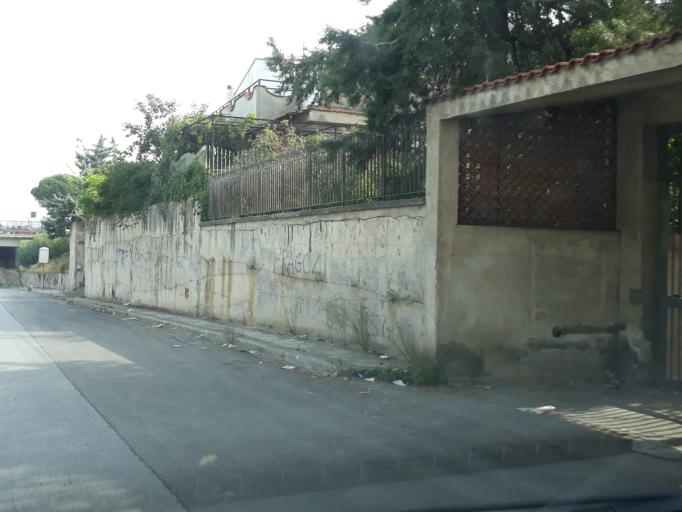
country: IT
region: Sicily
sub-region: Palermo
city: Villa Ciambra
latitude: 38.0876
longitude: 13.3455
